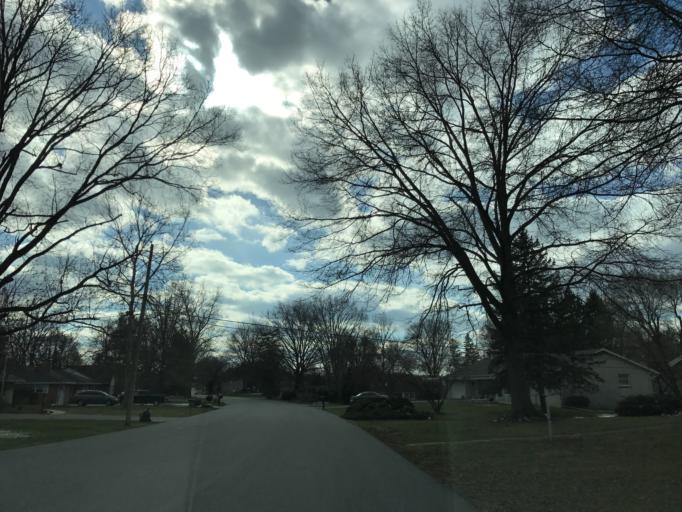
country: US
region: Pennsylvania
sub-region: Lancaster County
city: Elizabethtown
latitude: 40.1546
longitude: -76.5871
